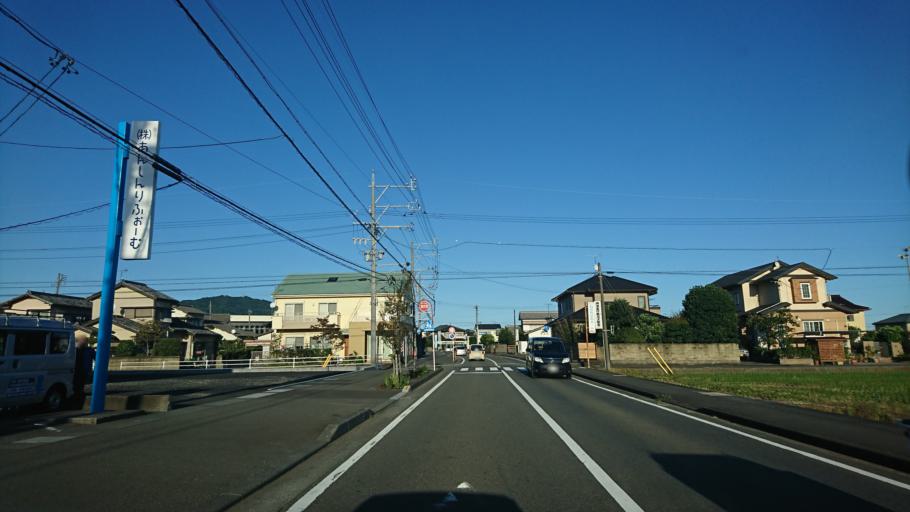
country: JP
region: Shizuoka
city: Fujieda
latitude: 34.8684
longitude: 138.2763
